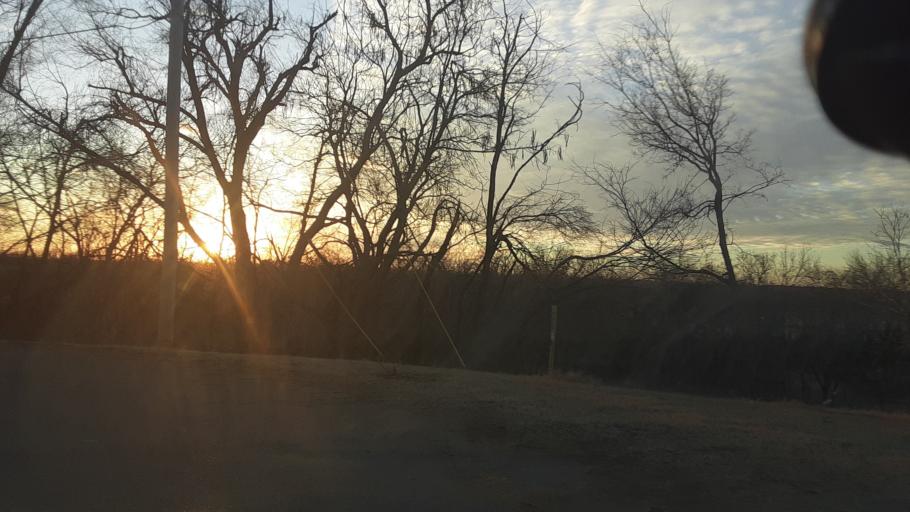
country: US
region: Oklahoma
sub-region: Logan County
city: Guthrie
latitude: 35.8812
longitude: -97.4274
